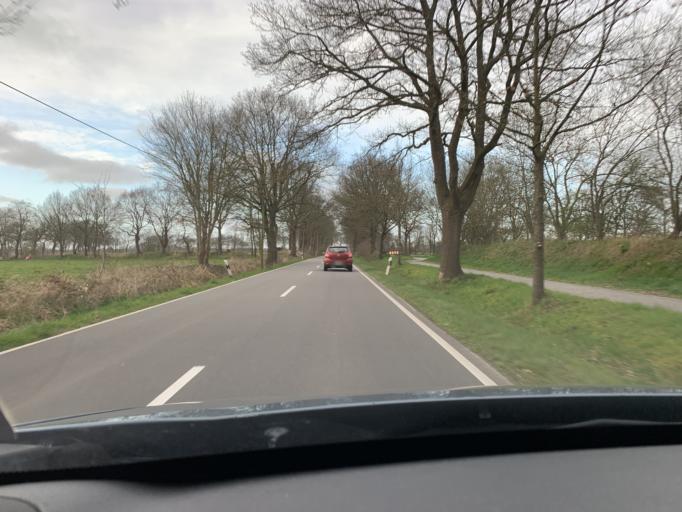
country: DE
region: Lower Saxony
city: Schwerinsdorf
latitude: 53.2637
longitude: 7.7082
